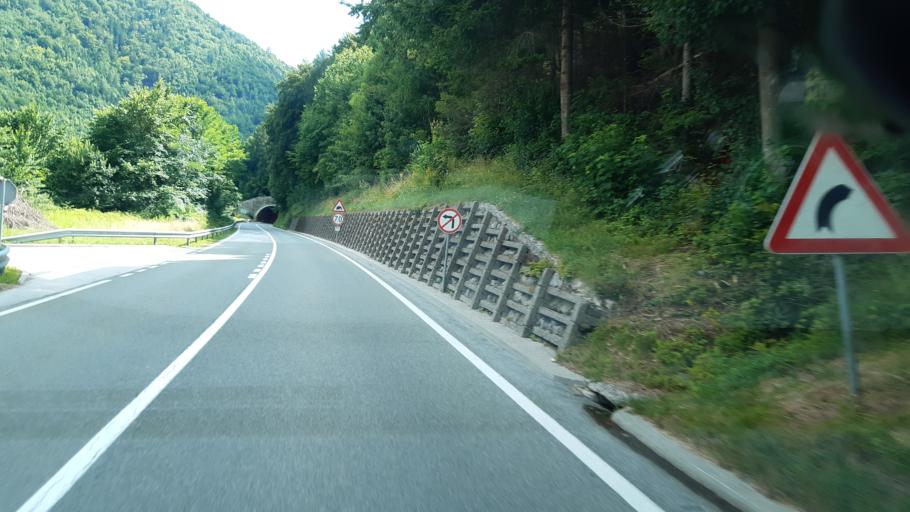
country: SI
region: Trzic
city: Trzic
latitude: 46.3654
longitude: 14.3059
